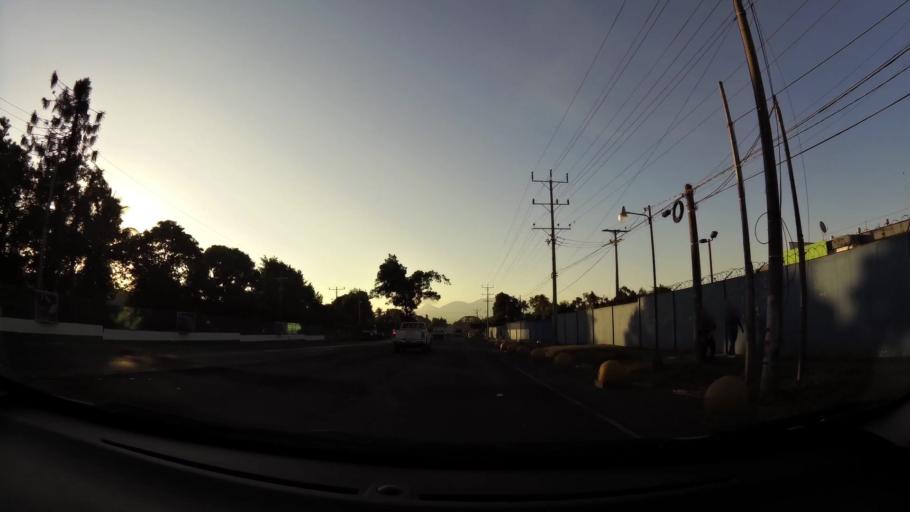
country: SV
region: Sonsonate
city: Armenia
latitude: 13.7379
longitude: -89.3993
